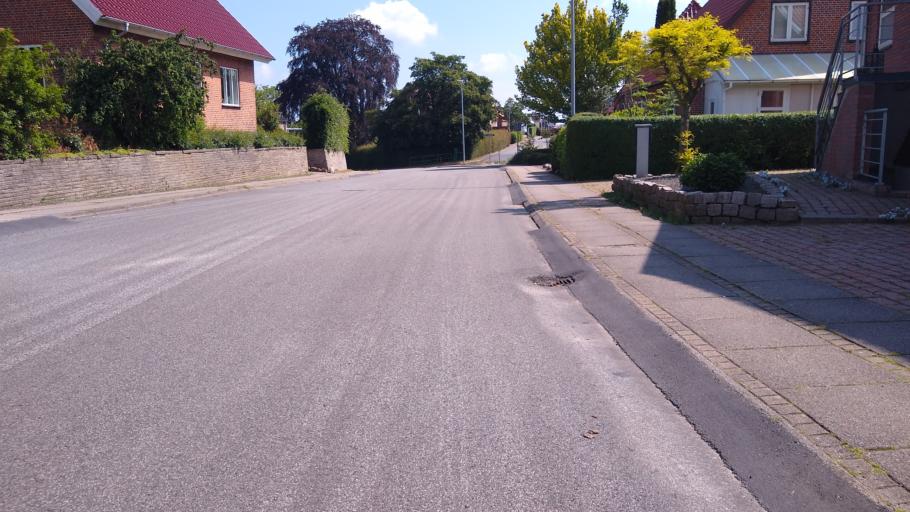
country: DK
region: South Denmark
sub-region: Vejle Kommune
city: Borkop
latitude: 55.6399
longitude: 9.6468
